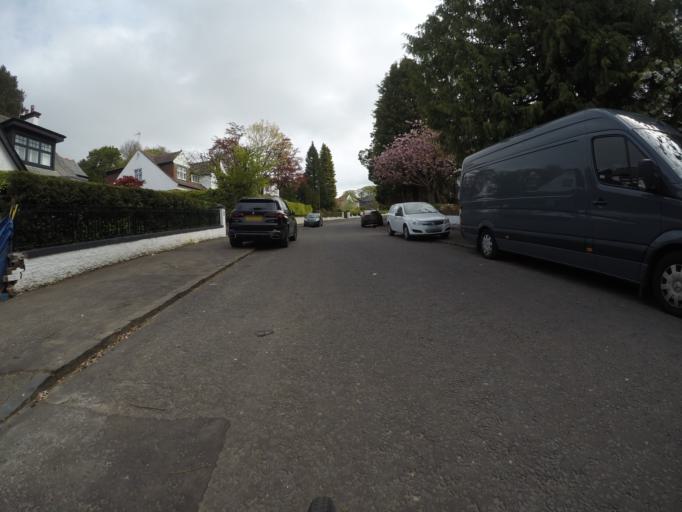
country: GB
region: Scotland
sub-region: East Renfrewshire
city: Giffnock
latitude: 55.7878
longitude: -4.3057
